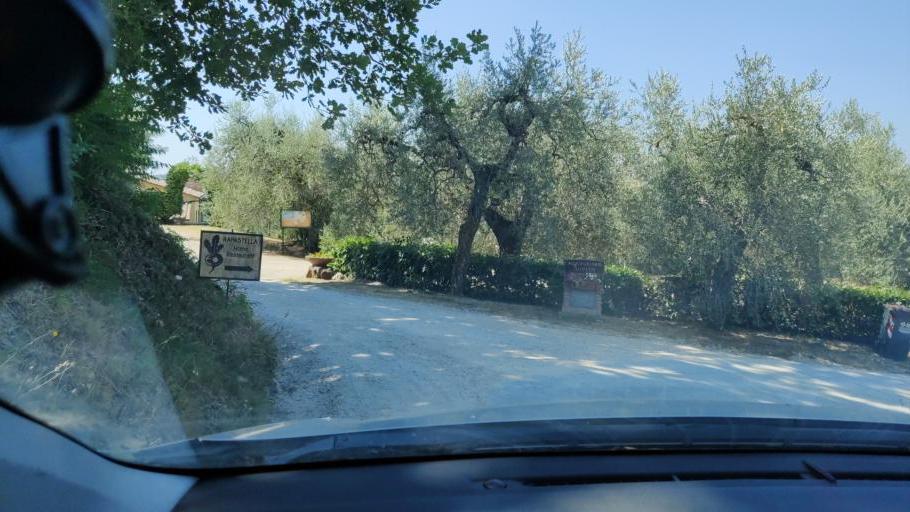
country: IT
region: Umbria
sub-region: Provincia di Terni
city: Amelia
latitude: 42.5455
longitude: 12.4338
